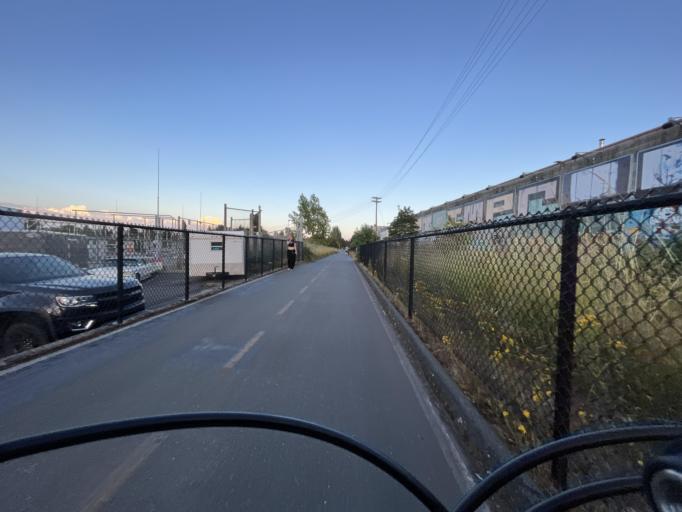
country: CA
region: British Columbia
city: Victoria
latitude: 48.4349
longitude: -123.3961
